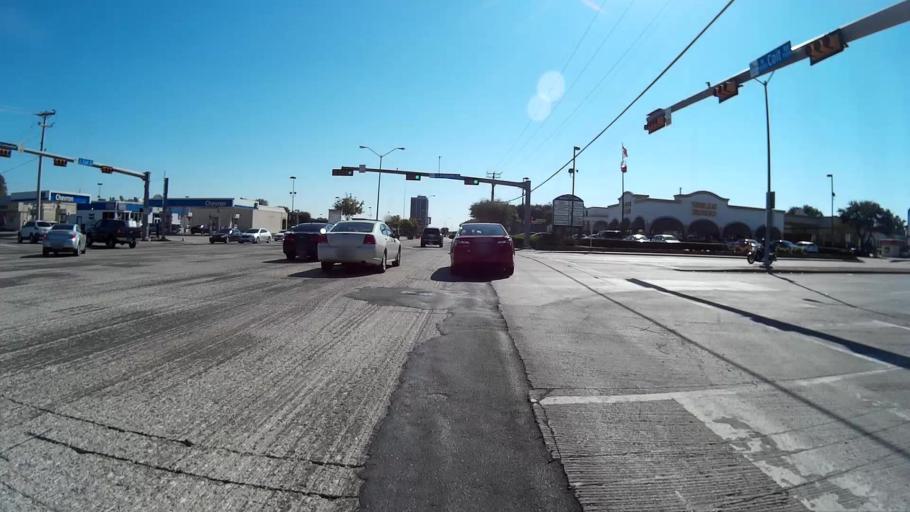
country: US
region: Texas
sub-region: Dallas County
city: Richardson
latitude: 32.9624
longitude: -96.7690
